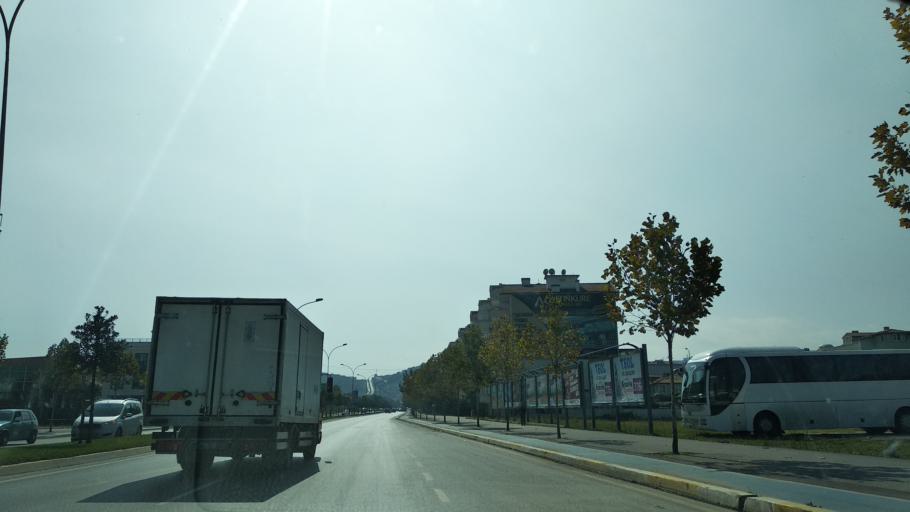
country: TR
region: Sakarya
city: Adapazari
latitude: 40.7713
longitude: 30.3641
